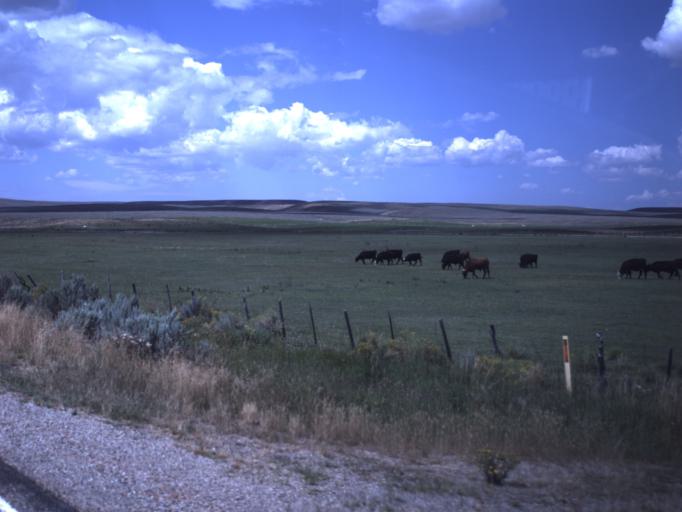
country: US
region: Utah
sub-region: Rich County
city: Randolph
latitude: 41.7730
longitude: -111.1172
